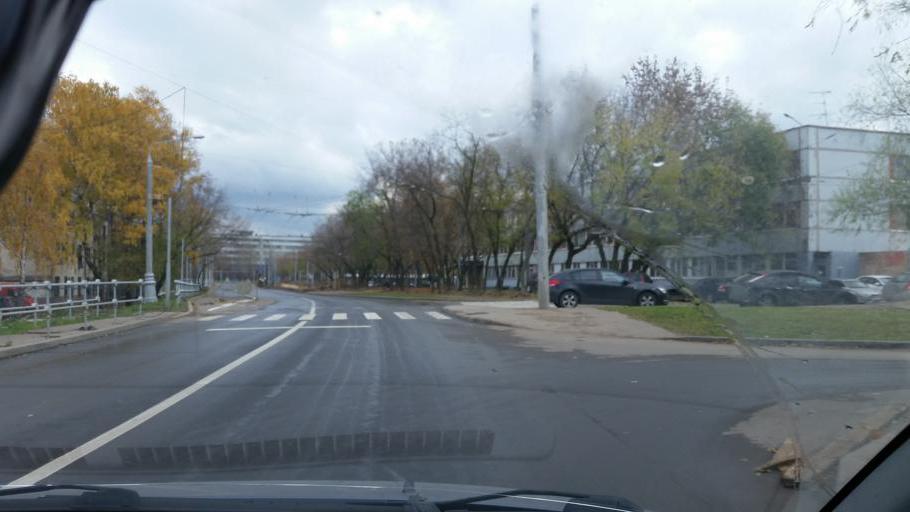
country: RU
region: Moscow
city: Kotlovka
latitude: 55.6725
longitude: 37.6172
